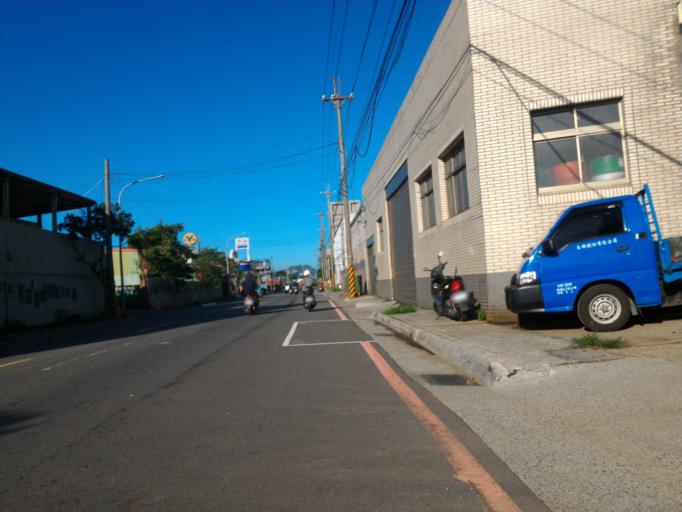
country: TW
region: Taipei
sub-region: Taipei
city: Banqiao
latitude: 24.9725
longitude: 121.4164
